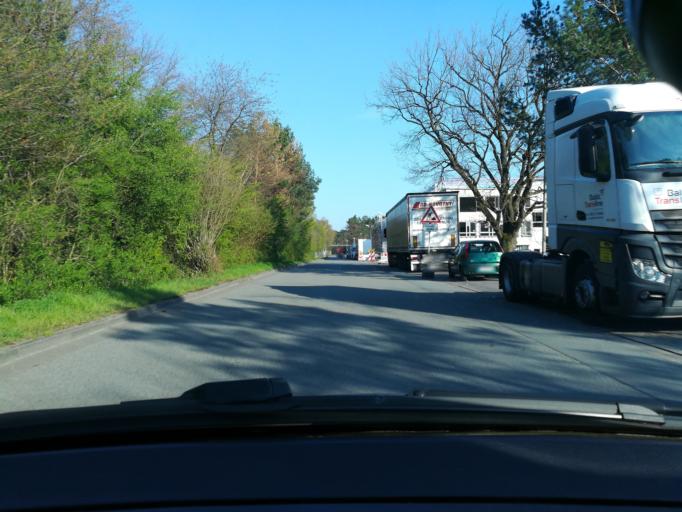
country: DE
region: North Rhine-Westphalia
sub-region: Regierungsbezirk Detmold
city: Verl
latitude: 51.9444
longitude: 8.5648
